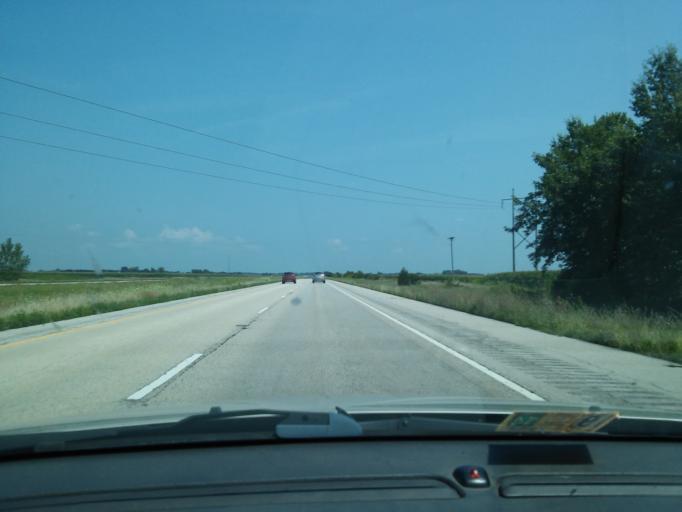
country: US
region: Illinois
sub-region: Sangamon County
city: New Berlin
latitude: 39.7368
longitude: -90.0147
